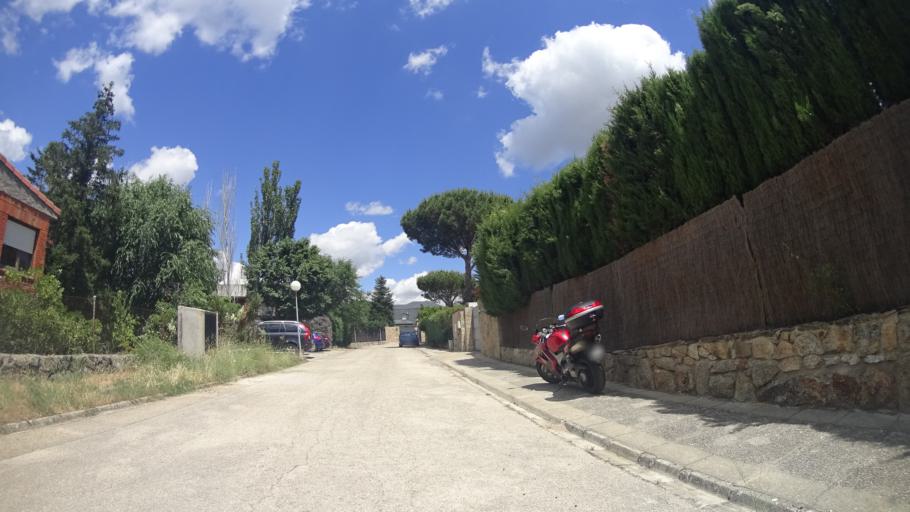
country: ES
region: Madrid
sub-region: Provincia de Madrid
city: Hoyo de Manzanares
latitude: 40.6115
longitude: -3.9320
